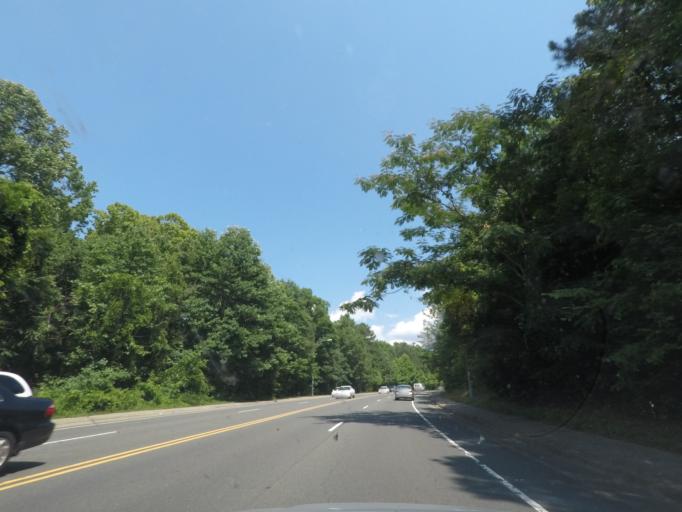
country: US
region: North Carolina
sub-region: Durham County
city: Durham
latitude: 35.9607
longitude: -78.9524
